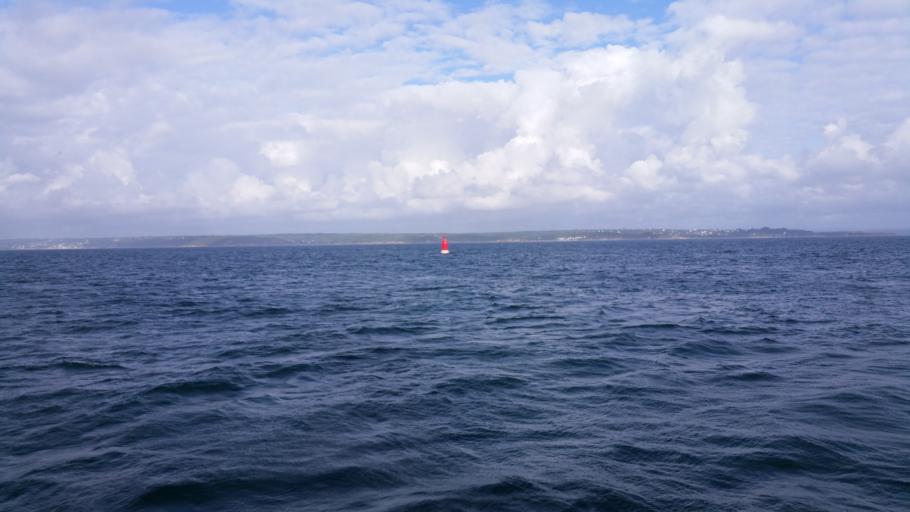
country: FR
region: Brittany
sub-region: Departement du Finistere
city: Brest
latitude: 48.3581
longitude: -4.5096
